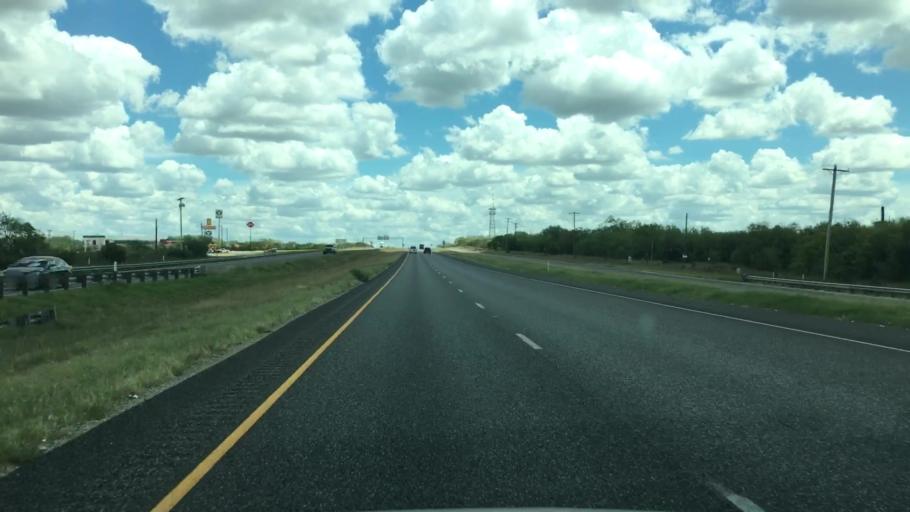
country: US
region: Texas
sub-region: Atascosa County
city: Pleasanton
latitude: 28.9055
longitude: -98.4291
